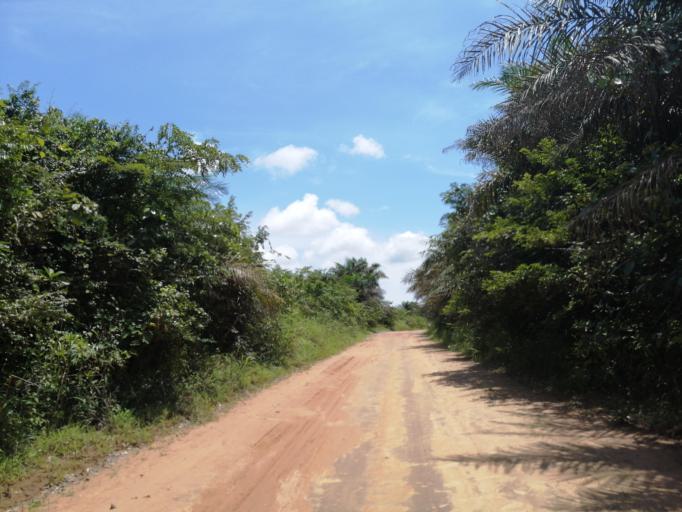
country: SL
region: Northern Province
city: Pepel
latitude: 8.6719
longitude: -13.0003
